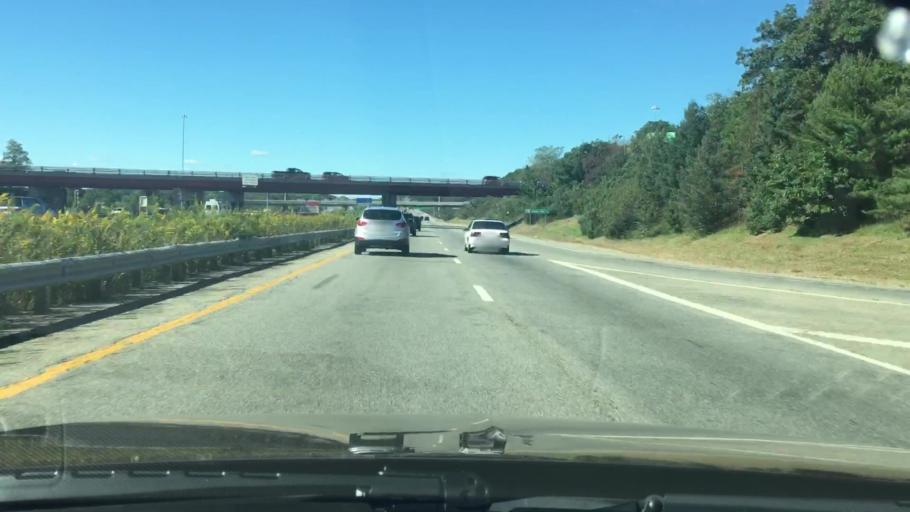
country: US
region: New York
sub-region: Suffolk County
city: Commack
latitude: 40.8052
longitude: -73.2793
